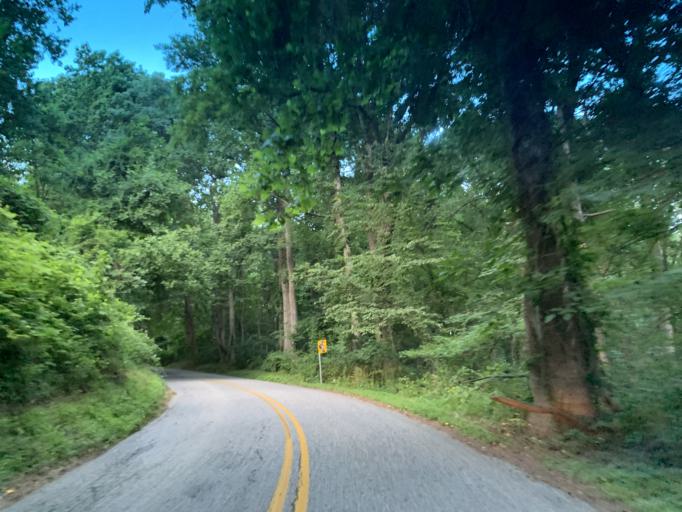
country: US
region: Maryland
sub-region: Harford County
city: Aberdeen
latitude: 39.5341
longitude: -76.1569
